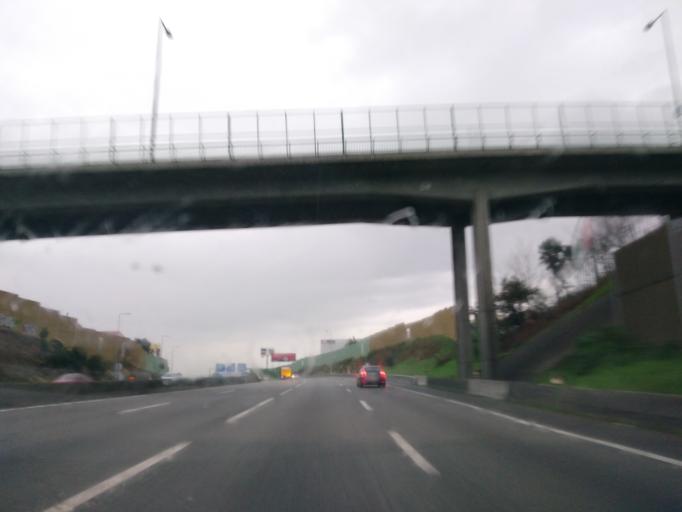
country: PT
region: Porto
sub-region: Maia
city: Pedroucos
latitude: 41.1908
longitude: -8.5934
